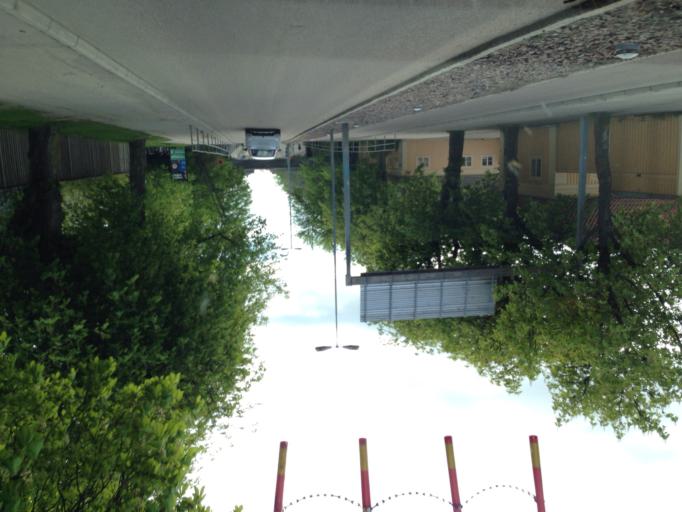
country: SE
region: Soedermanland
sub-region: Nykopings Kommun
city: Nykoping
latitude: 58.7581
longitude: 16.9996
